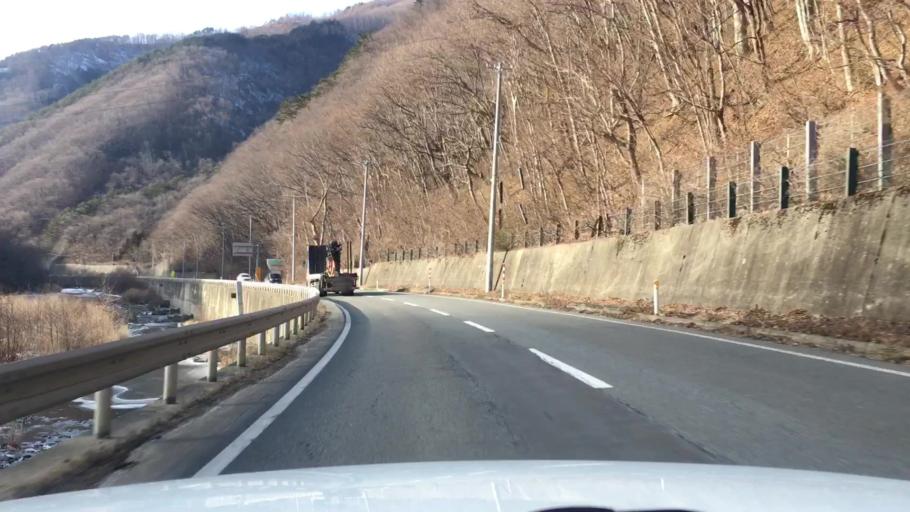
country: JP
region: Iwate
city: Tono
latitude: 39.6489
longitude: 141.5846
